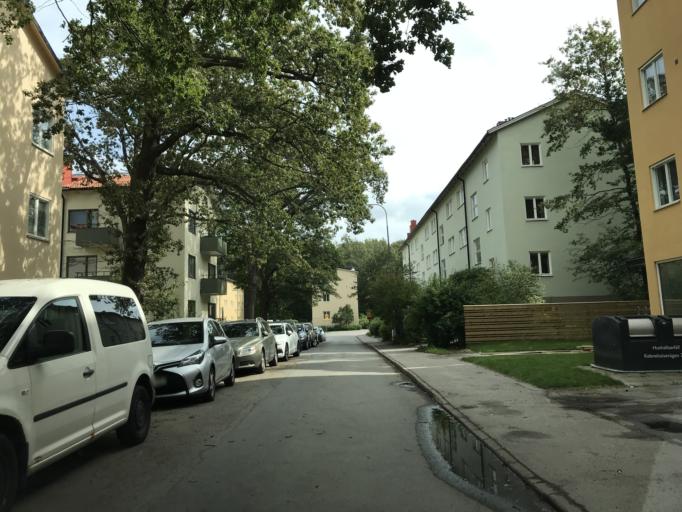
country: SE
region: Stockholm
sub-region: Sundbybergs Kommun
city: Sundbyberg
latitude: 59.3387
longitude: 17.9768
